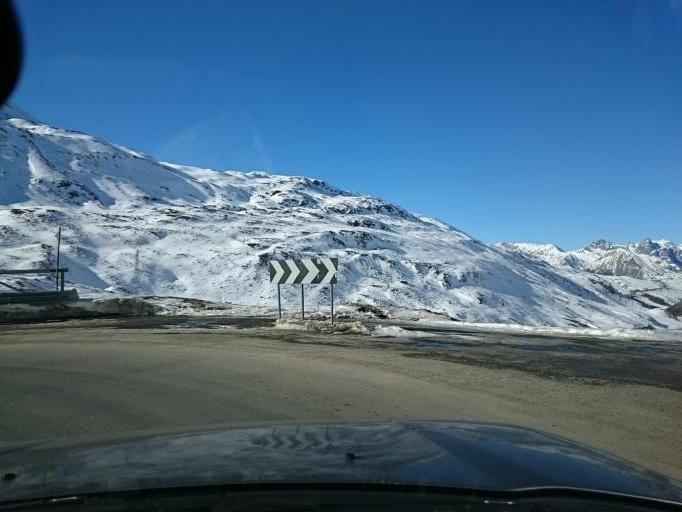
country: IT
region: Lombardy
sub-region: Provincia di Sondrio
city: Livigno
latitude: 46.4997
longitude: 10.2063
